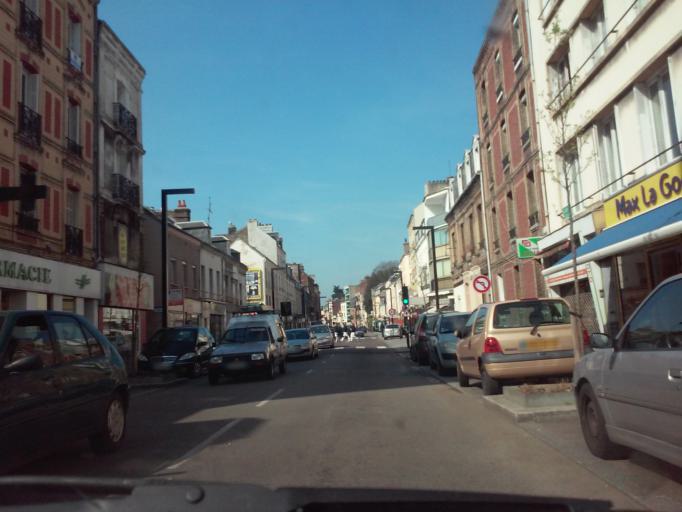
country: FR
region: Haute-Normandie
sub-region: Departement de la Seine-Maritime
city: Le Havre
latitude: 49.4998
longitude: 0.1272
